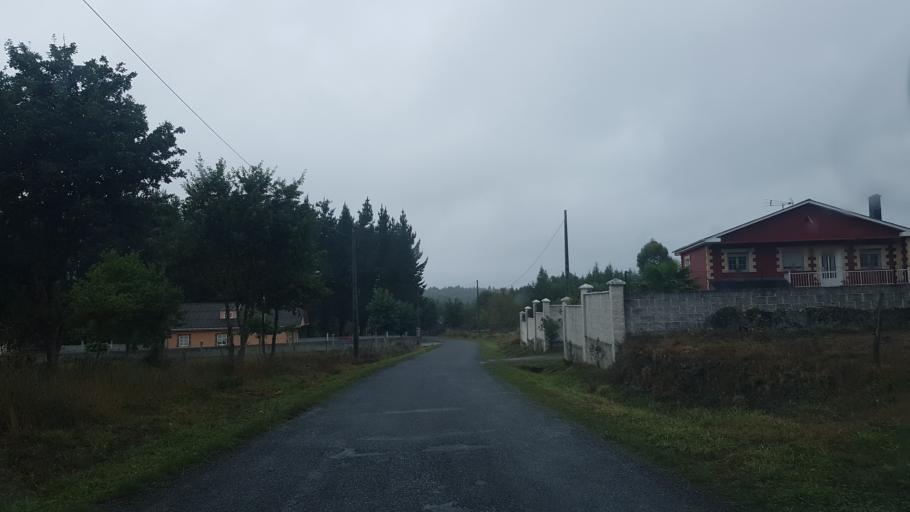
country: ES
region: Galicia
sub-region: Provincia de Lugo
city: Friol
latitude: 43.1174
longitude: -7.8160
